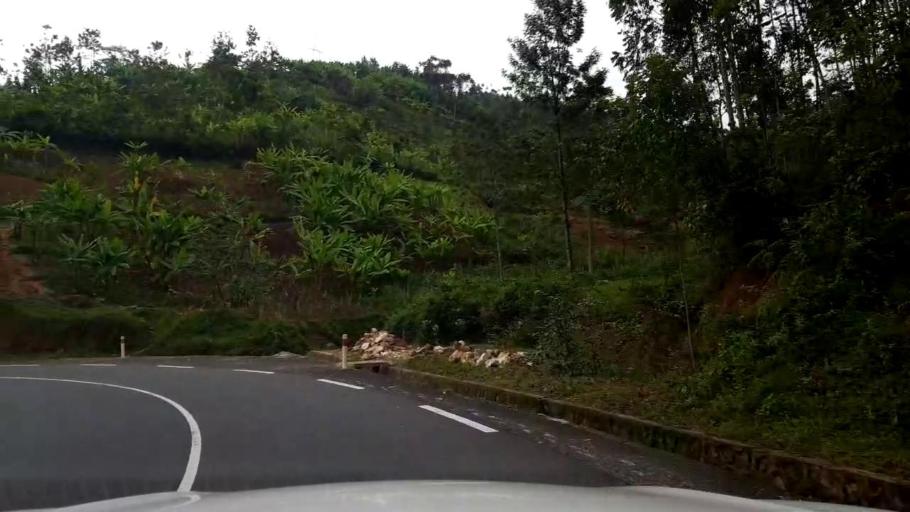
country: RW
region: Western Province
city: Kibuye
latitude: -1.9067
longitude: 29.3614
